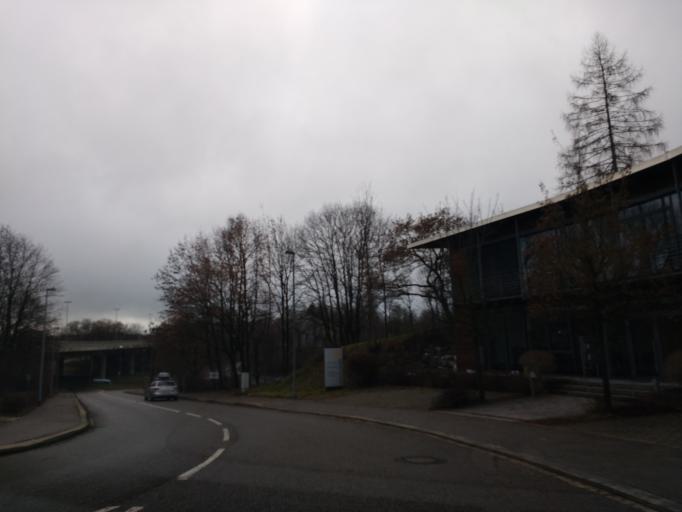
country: DE
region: Bavaria
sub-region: Swabia
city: Kempten (Allgaeu)
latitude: 47.7165
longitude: 10.3273
